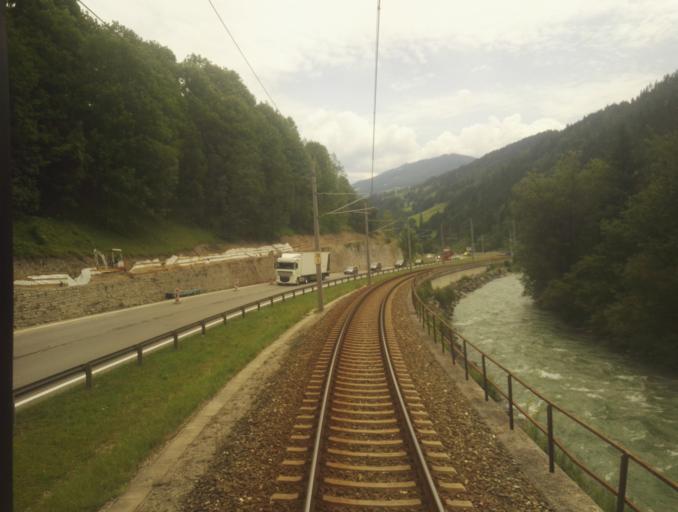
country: AT
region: Styria
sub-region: Politischer Bezirk Liezen
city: Schladming
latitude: 47.3896
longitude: 13.6345
